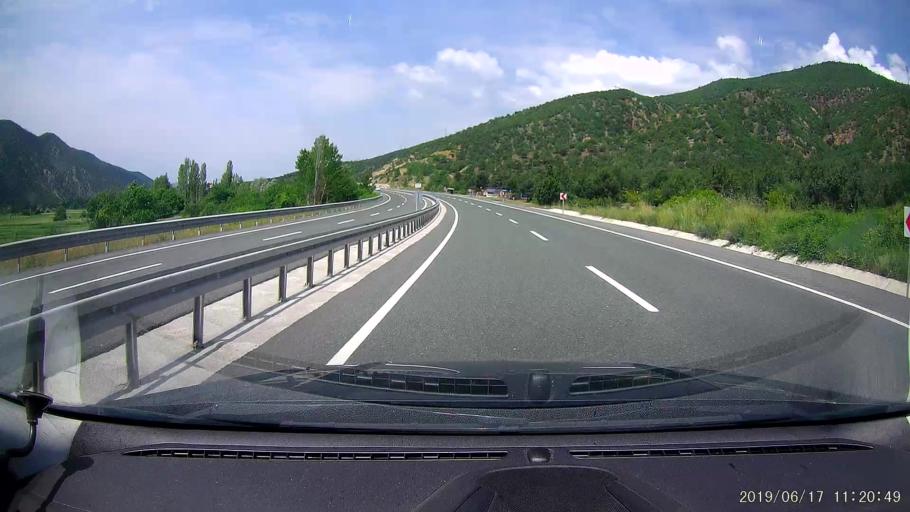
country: TR
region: Cankiri
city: Yaprakli
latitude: 40.9128
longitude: 33.7975
